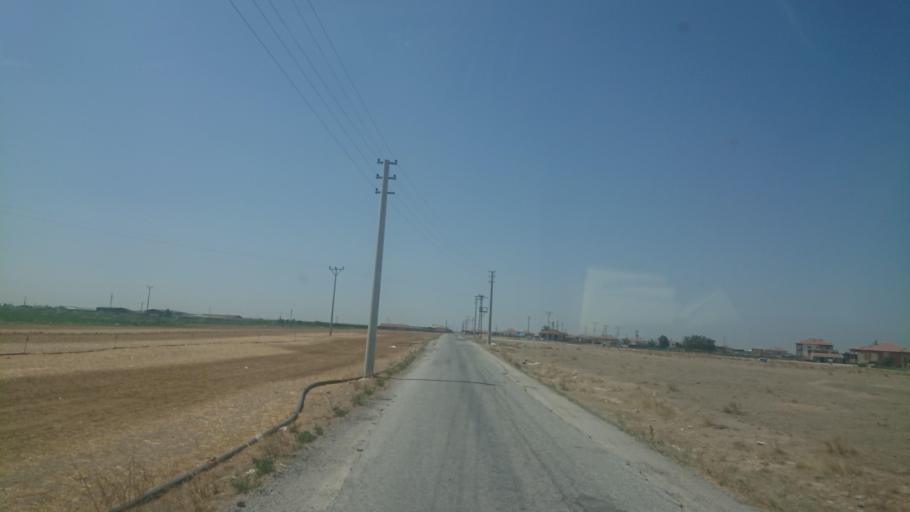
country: TR
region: Aksaray
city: Yesilova
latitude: 38.2911
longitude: 33.7200
